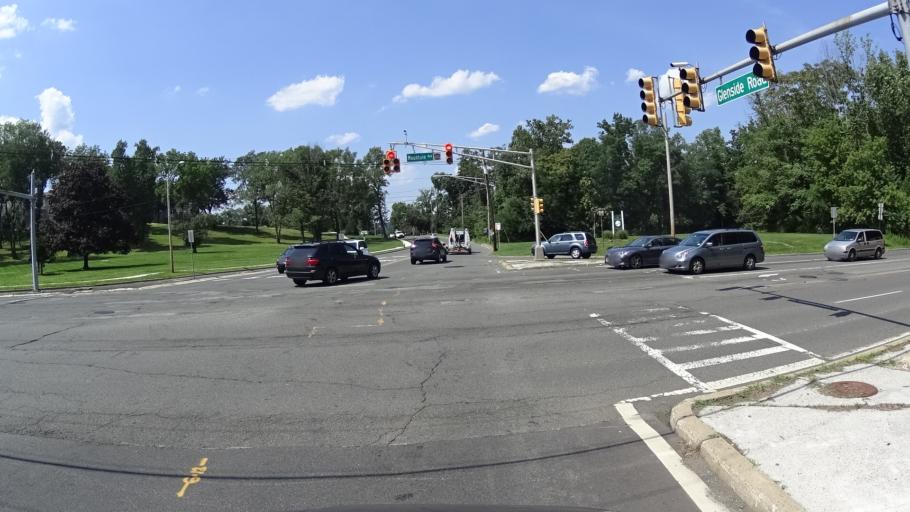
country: US
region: New Jersey
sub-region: Union County
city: New Providence
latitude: 40.6877
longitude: -74.3972
